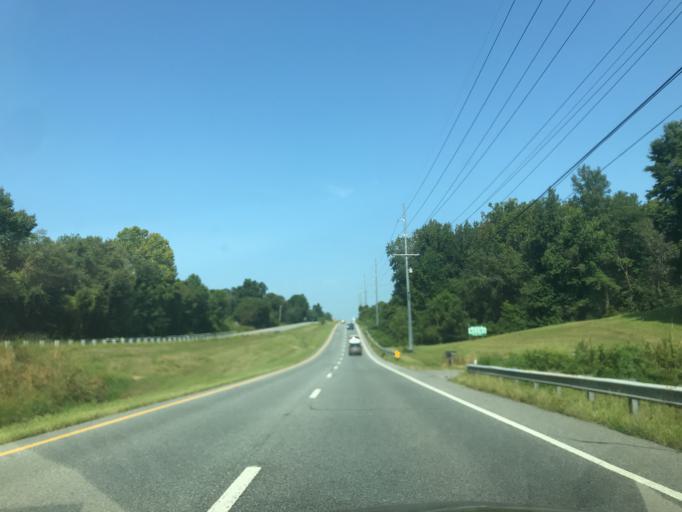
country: US
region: Maryland
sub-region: Calvert County
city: Huntingtown Town Center
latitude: 38.6685
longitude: -76.6159
